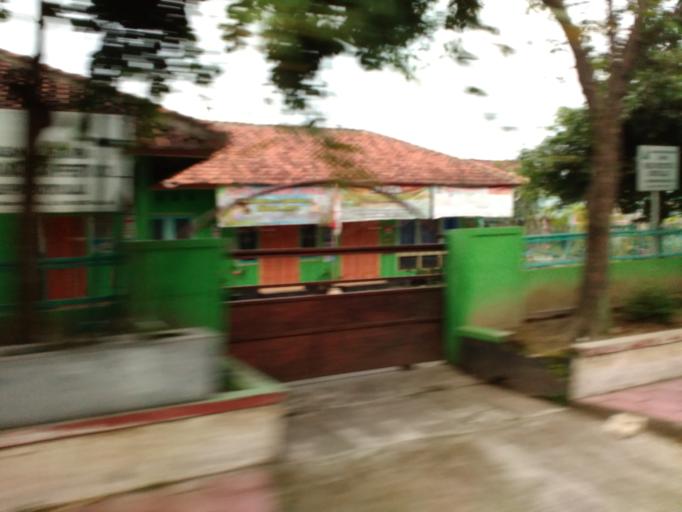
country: ID
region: Central Java
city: Boyolali
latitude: -7.5317
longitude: 110.5991
